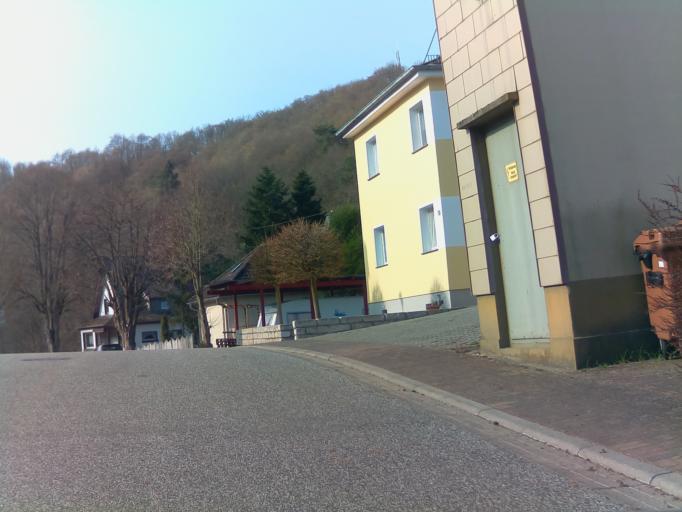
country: DE
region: Rheinland-Pfalz
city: Kronweiler
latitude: 49.6563
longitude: 7.2613
